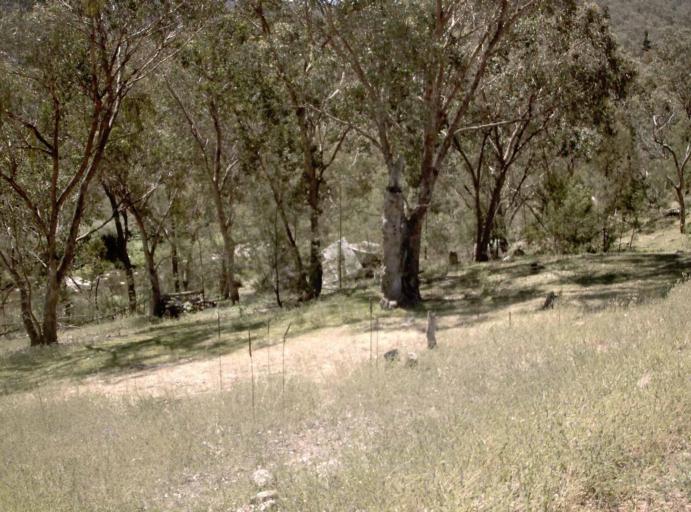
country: AU
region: New South Wales
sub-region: Snowy River
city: Jindabyne
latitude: -37.0662
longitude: 148.5148
